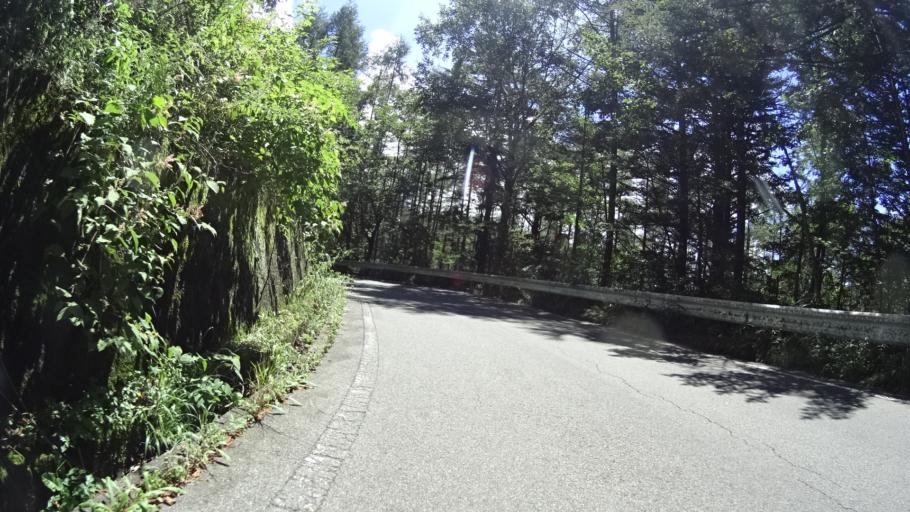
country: JP
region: Yamanashi
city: Enzan
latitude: 35.7307
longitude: 138.8429
